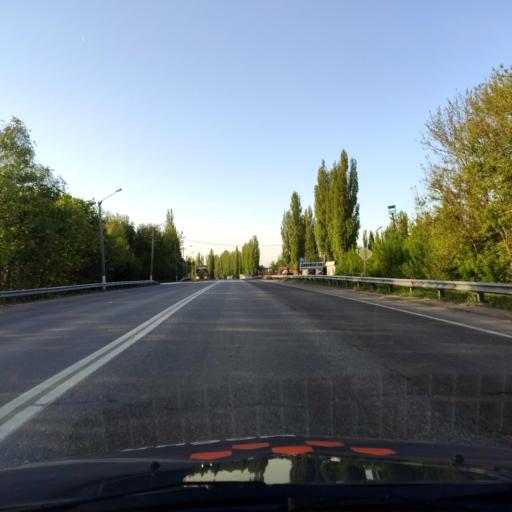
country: RU
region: Lipetsk
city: Yelets
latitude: 52.6109
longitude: 38.4628
